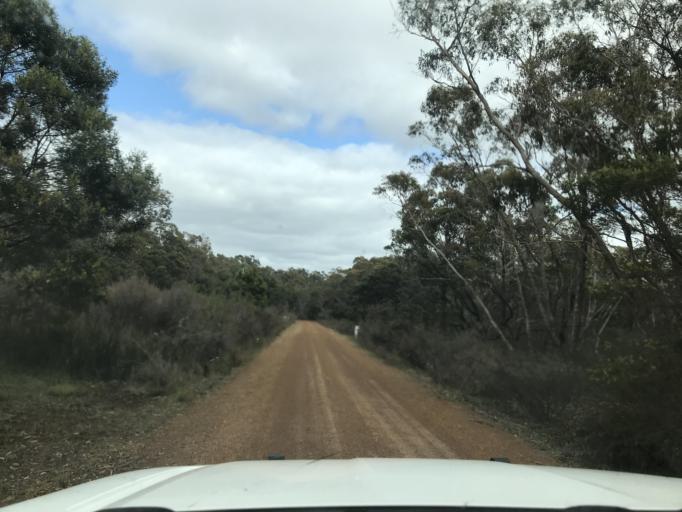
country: AU
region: South Australia
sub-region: Wattle Range
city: Penola
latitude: -37.3344
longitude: 141.4124
